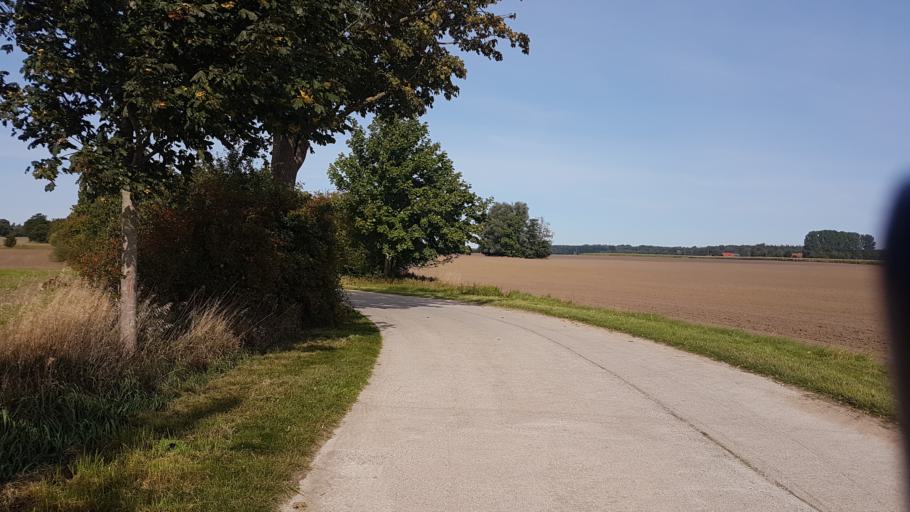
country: DE
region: Mecklenburg-Vorpommern
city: Gingst
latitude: 54.4122
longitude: 13.2580
